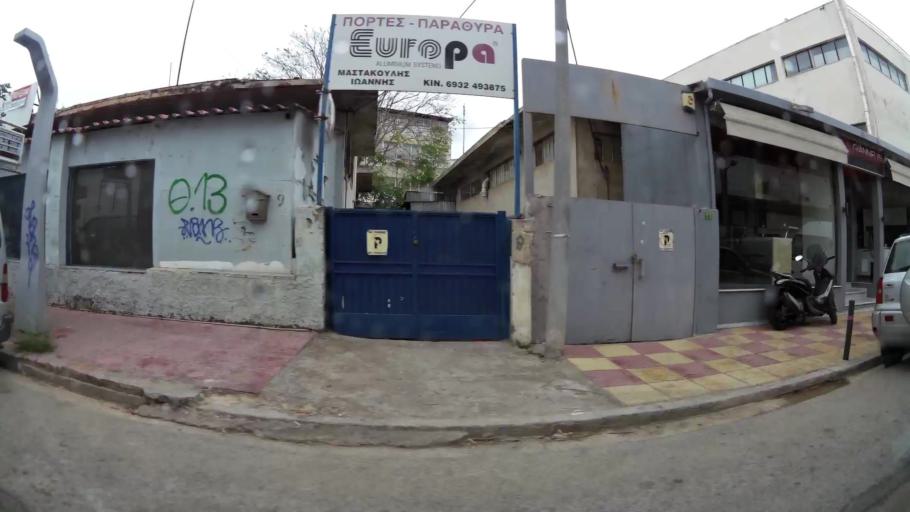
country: GR
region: Attica
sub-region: Nomarchia Athinas
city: Peristeri
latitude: 38.0068
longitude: 23.7076
